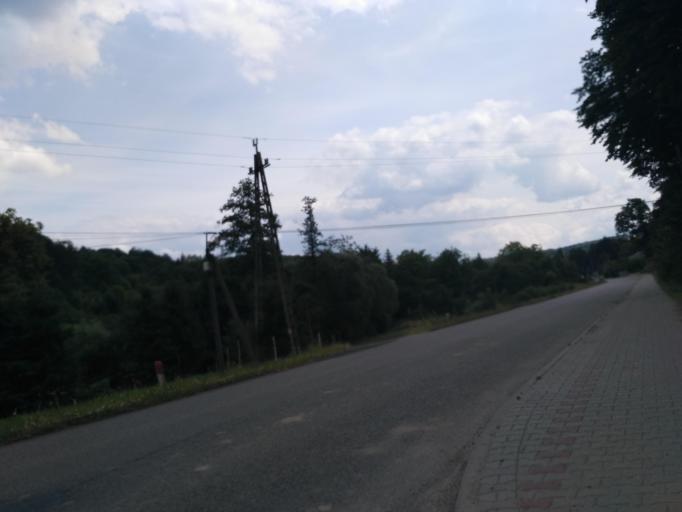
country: PL
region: Subcarpathian Voivodeship
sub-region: Powiat debicki
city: Brzeznica
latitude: 50.0448
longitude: 21.4885
